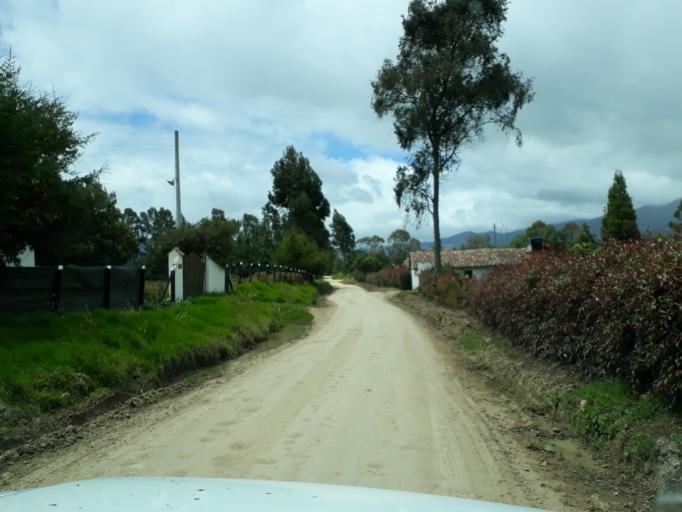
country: CO
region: Cundinamarca
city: Guasca
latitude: 4.8544
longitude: -73.8981
